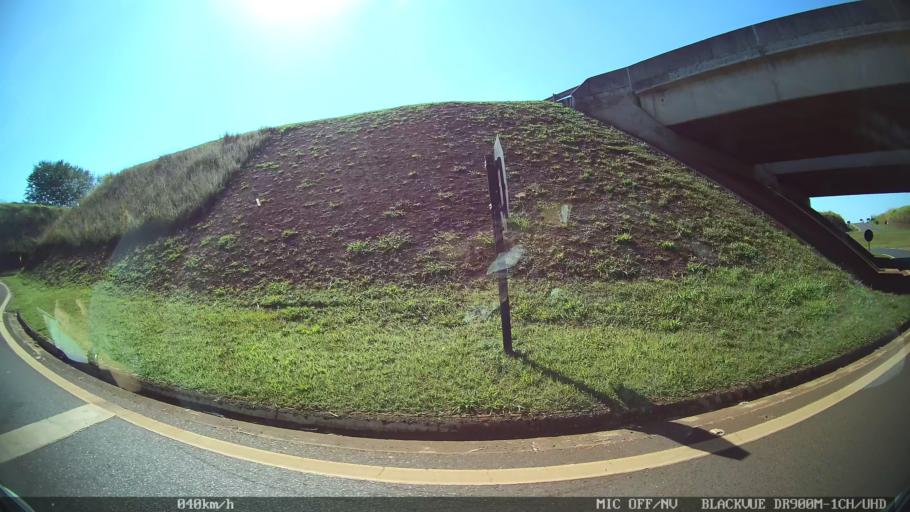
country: BR
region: Sao Paulo
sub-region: Franca
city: Franca
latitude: -20.6768
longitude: -47.4958
